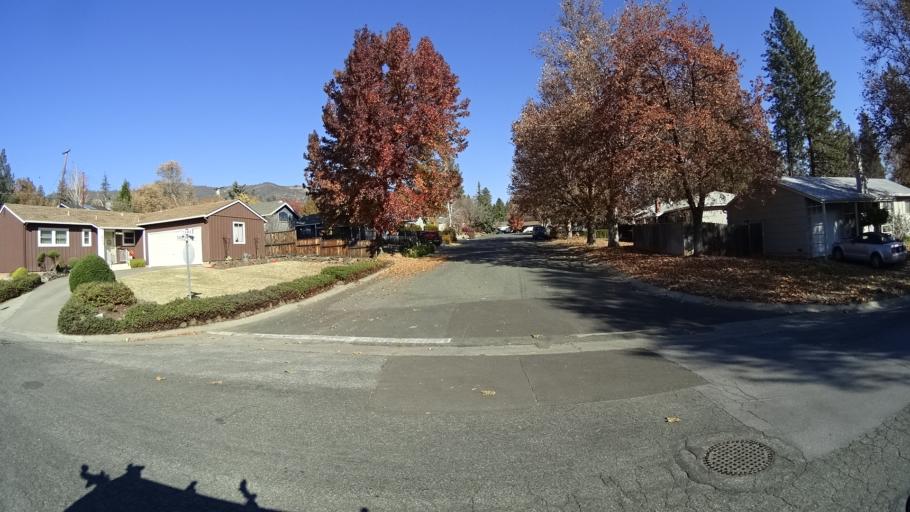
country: US
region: California
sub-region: Siskiyou County
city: Yreka
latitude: 41.7362
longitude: -122.6489
